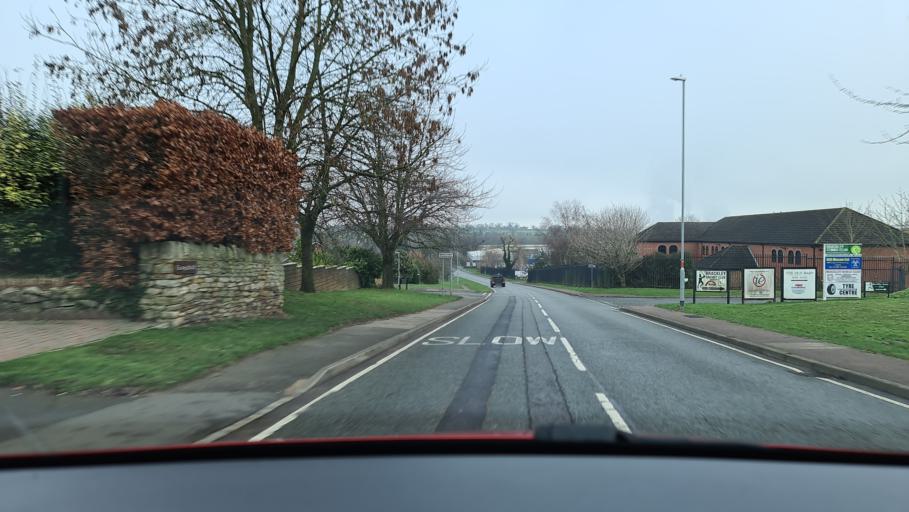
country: GB
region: England
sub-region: Northamptonshire
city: Brackley
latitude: 52.0289
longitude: -1.1430
